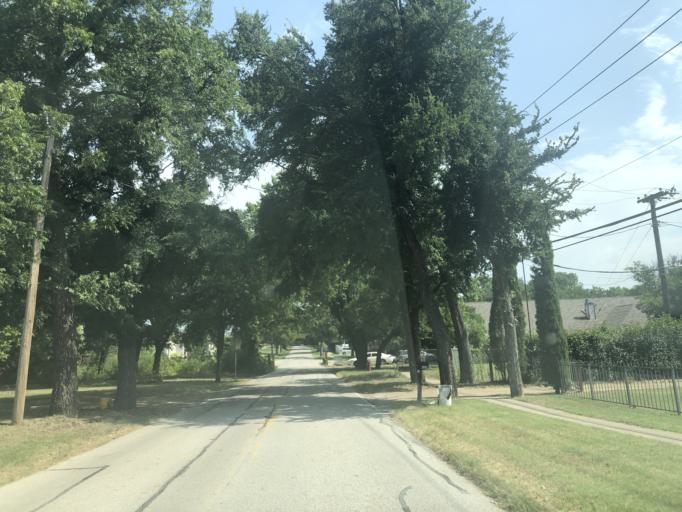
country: US
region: Texas
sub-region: Dallas County
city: Grand Prairie
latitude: 32.7724
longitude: -97.0430
